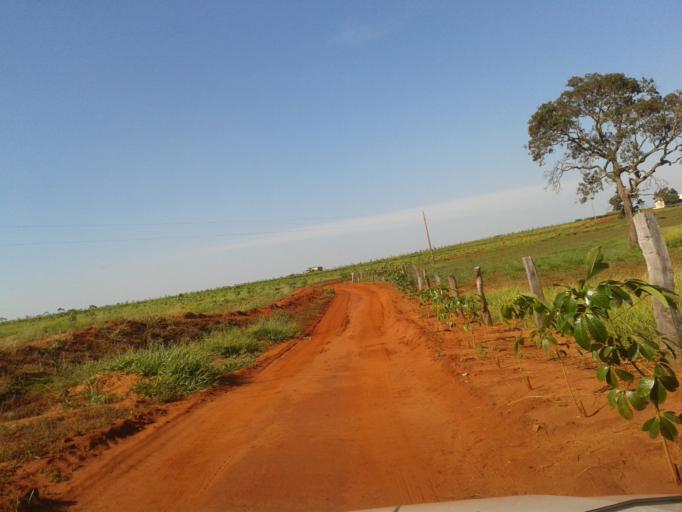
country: BR
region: Minas Gerais
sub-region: Campina Verde
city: Campina Verde
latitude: -19.4542
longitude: -49.6808
